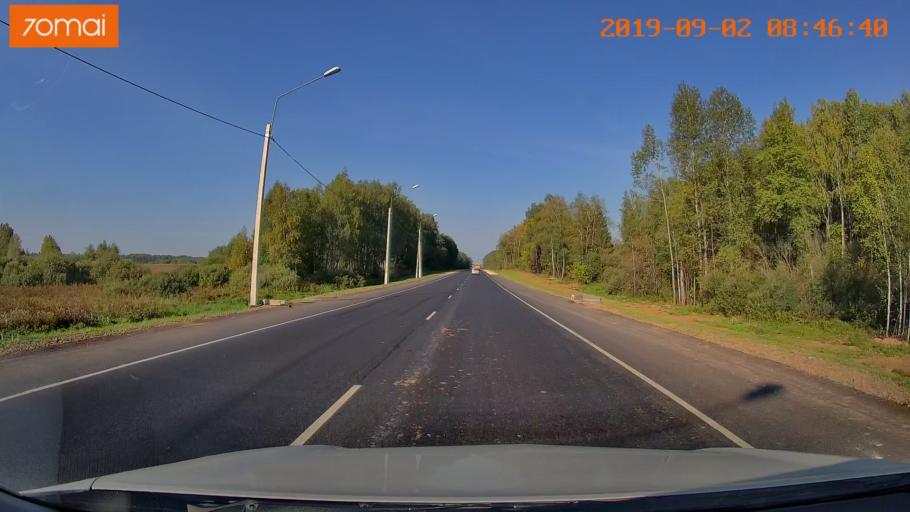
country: RU
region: Kaluga
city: Medyn'
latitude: 54.9685
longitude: 35.9726
